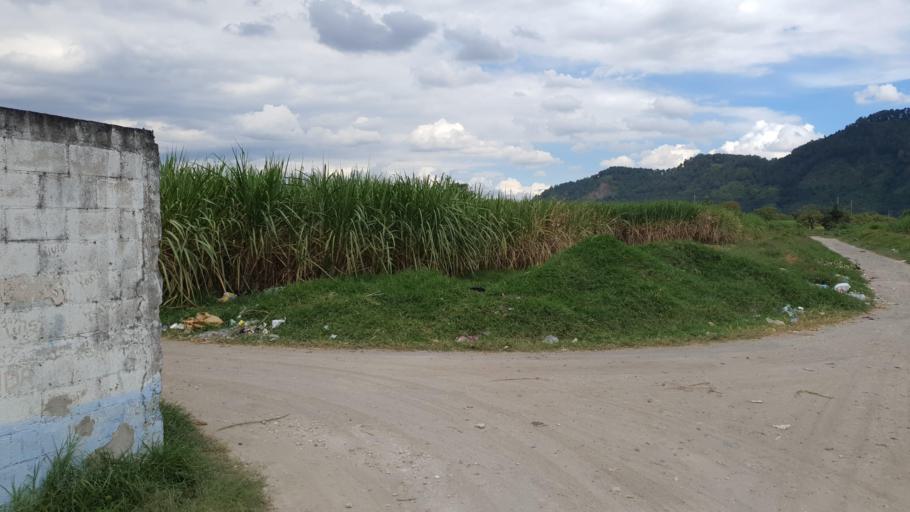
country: GT
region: Guatemala
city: Villa Canales
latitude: 14.4573
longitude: -90.5559
